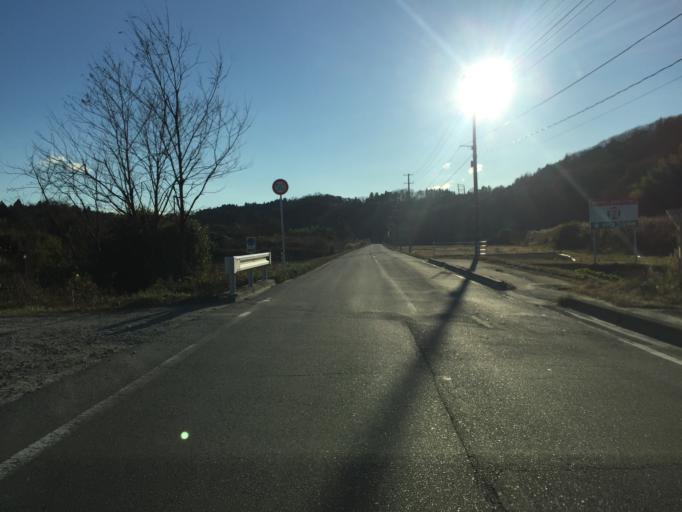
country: JP
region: Fukushima
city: Iwaki
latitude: 37.1026
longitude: 140.8621
